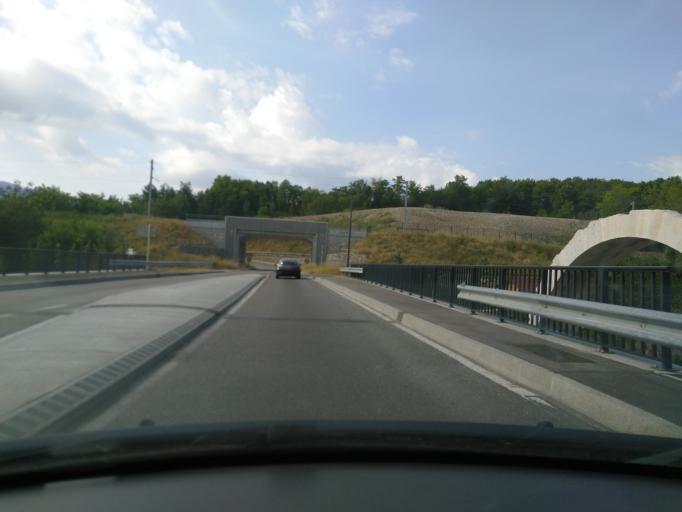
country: FR
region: Rhone-Alpes
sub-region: Departement de la Haute-Savoie
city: Saint-Julien-en-Genevois
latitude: 46.1389
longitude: 6.0733
